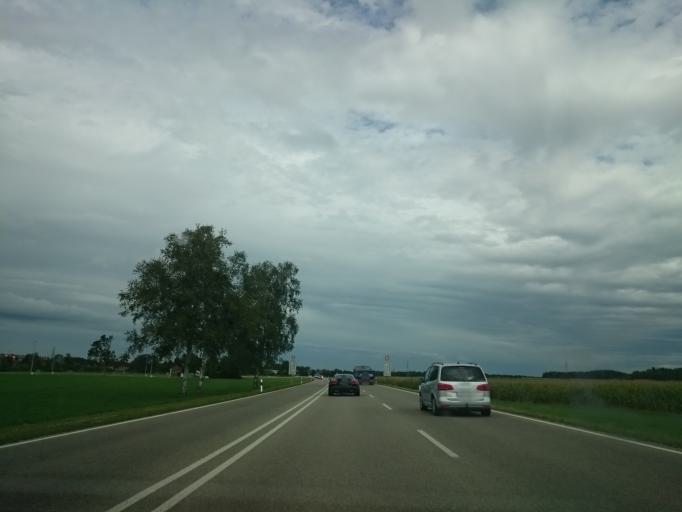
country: DE
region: Bavaria
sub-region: Swabia
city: Jengen
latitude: 48.0109
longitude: 10.7232
